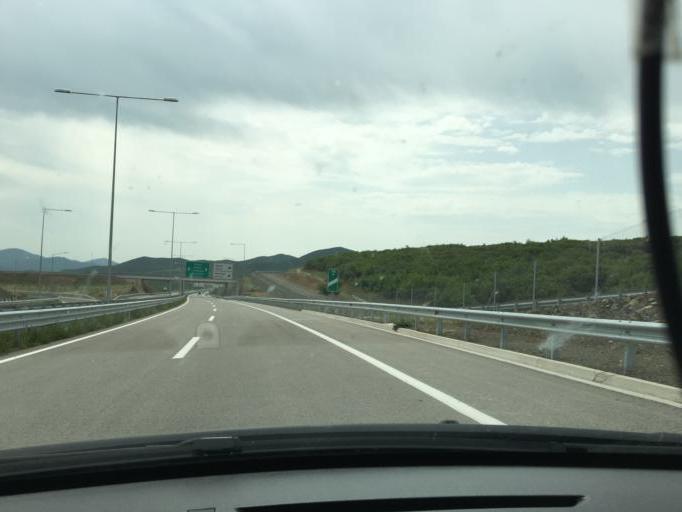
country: MK
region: Gevgelija
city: Miravci
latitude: 41.2998
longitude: 22.4290
